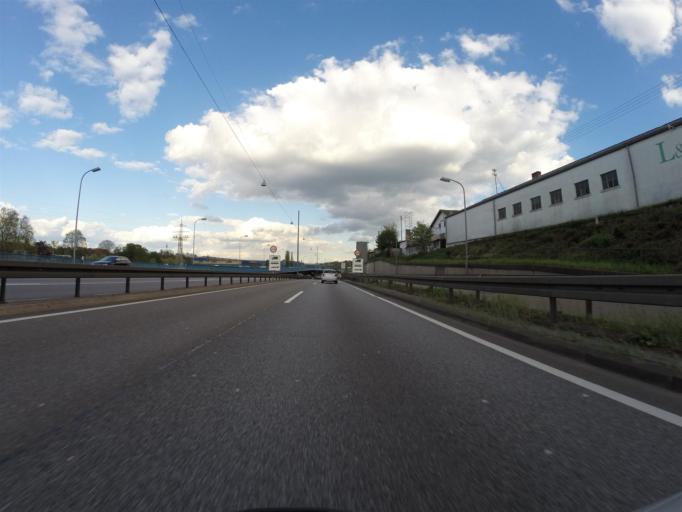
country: FR
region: Lorraine
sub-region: Departement de la Moselle
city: Schoeneck
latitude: 49.2381
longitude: 6.9404
